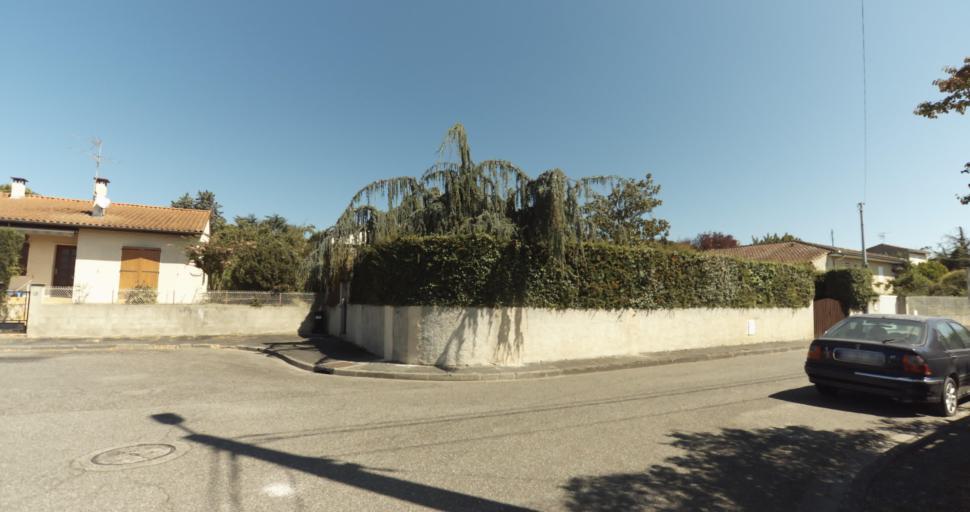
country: FR
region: Midi-Pyrenees
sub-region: Departement de la Haute-Garonne
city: L'Union
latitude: 43.6508
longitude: 1.4894
